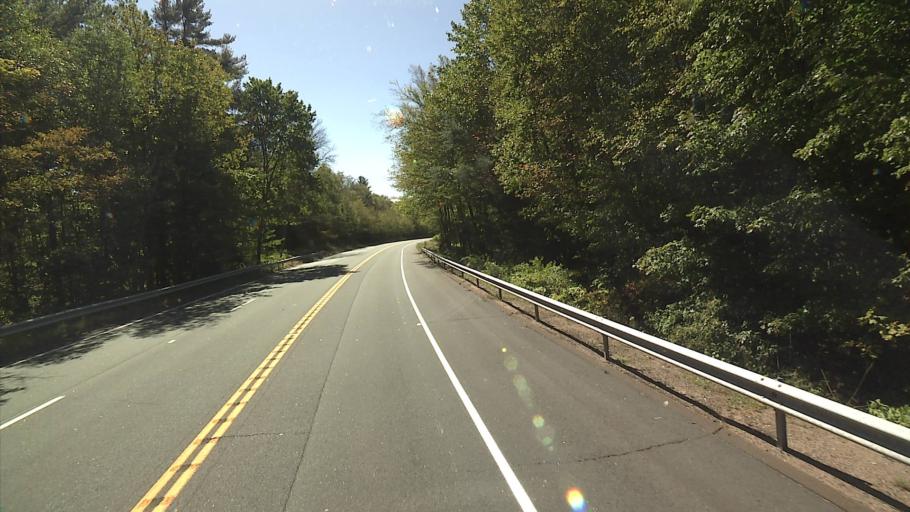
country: US
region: Connecticut
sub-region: New Haven County
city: Woodbridge
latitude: 41.3916
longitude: -72.9720
